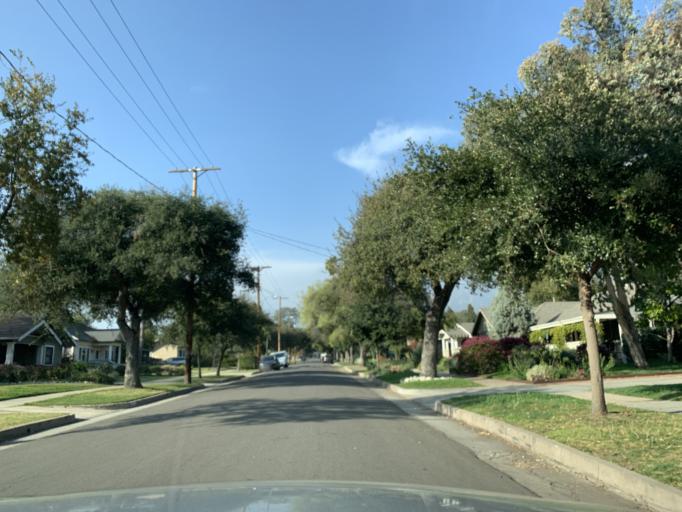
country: US
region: California
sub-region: Los Angeles County
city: Pasadena
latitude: 34.1592
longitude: -118.1244
